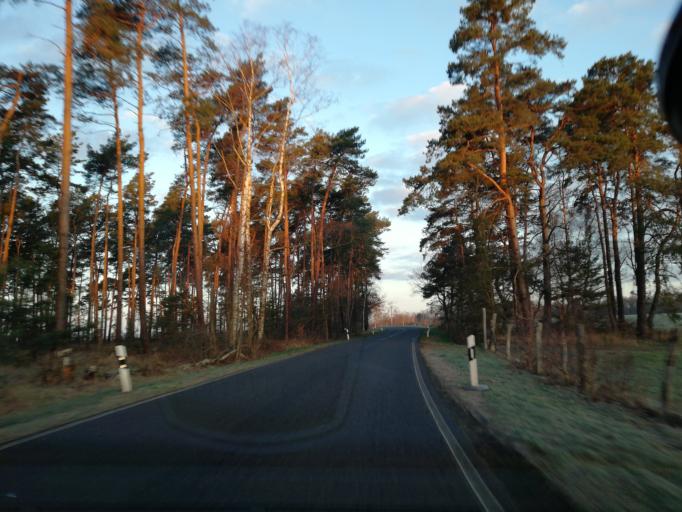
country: DE
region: Brandenburg
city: Bronkow
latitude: 51.7206
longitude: 13.8688
